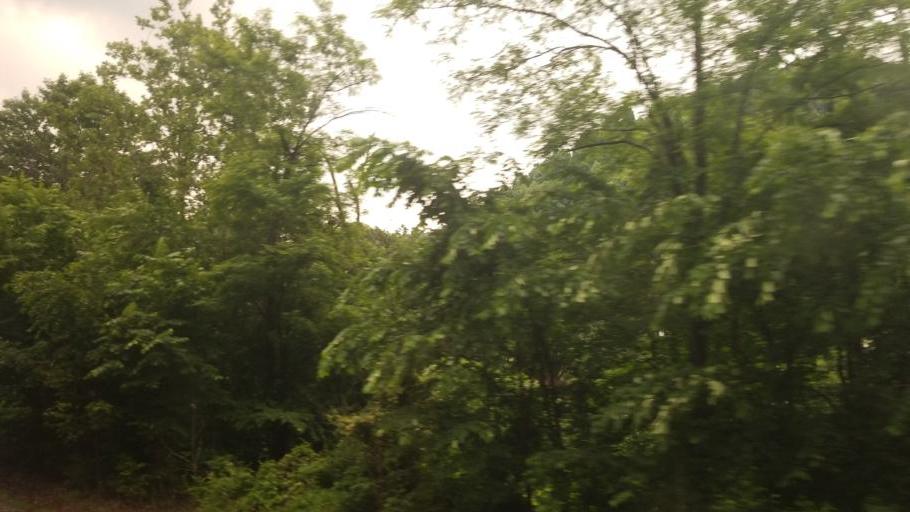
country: US
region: Maryland
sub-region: Allegany County
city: Cumberland
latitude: 39.8359
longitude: -78.7465
